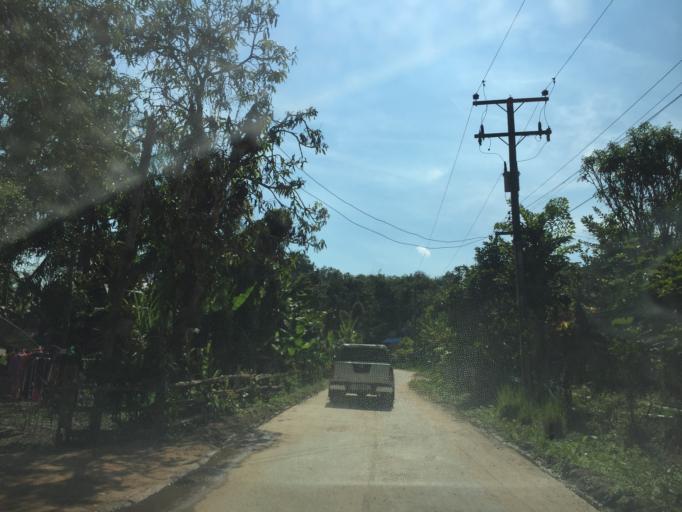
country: TH
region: Chiang Mai
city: Samoeng
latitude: 18.9911
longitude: 98.7264
